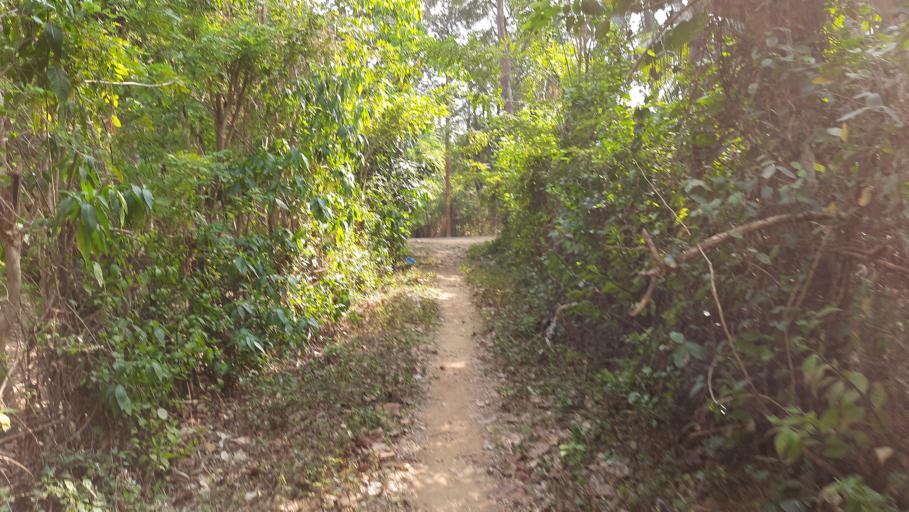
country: IN
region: Kerala
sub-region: Palakkad district
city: Ottappalam
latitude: 10.7180
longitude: 76.4768
